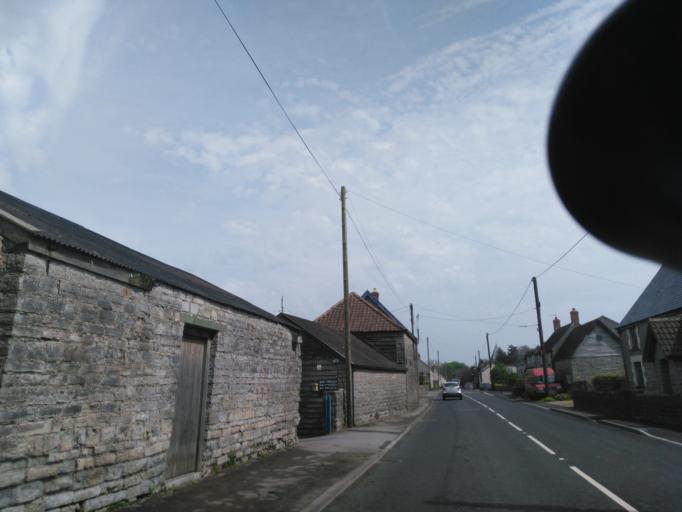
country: GB
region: England
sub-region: Somerset
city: Street
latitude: 51.1237
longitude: -2.7752
